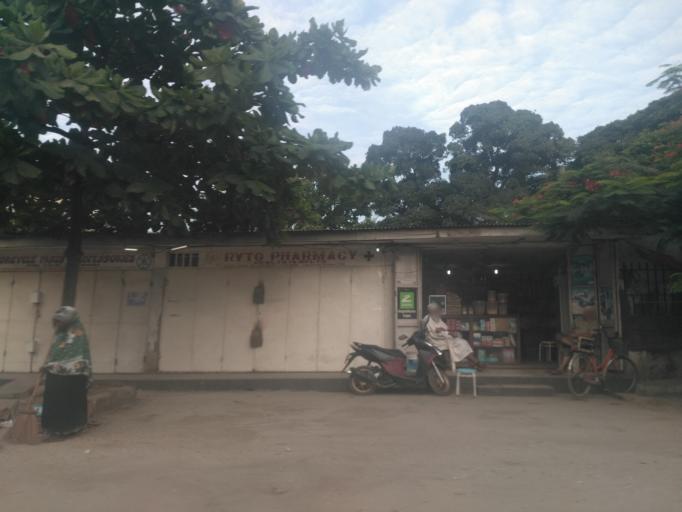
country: TZ
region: Zanzibar Urban/West
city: Zanzibar
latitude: -6.1638
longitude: 39.1934
